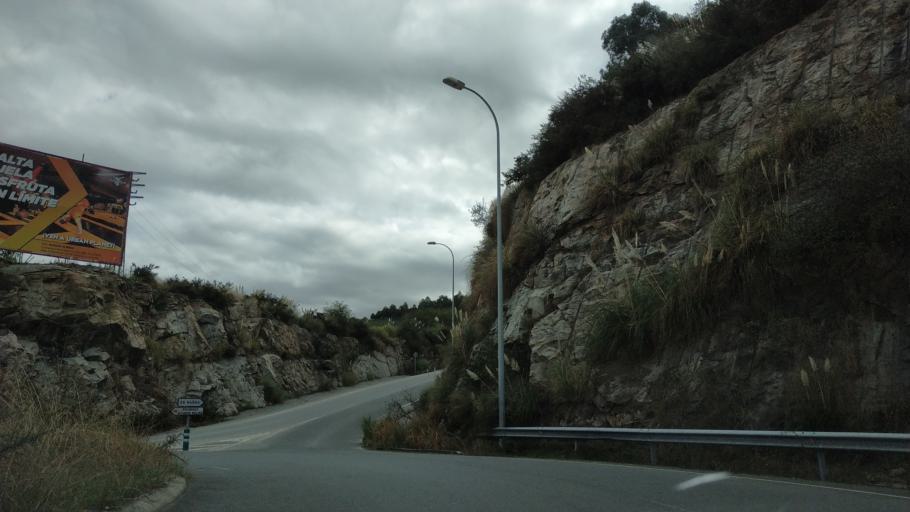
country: ES
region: Galicia
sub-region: Provincia da Coruna
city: A Coruna
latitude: 43.3404
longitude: -8.4285
